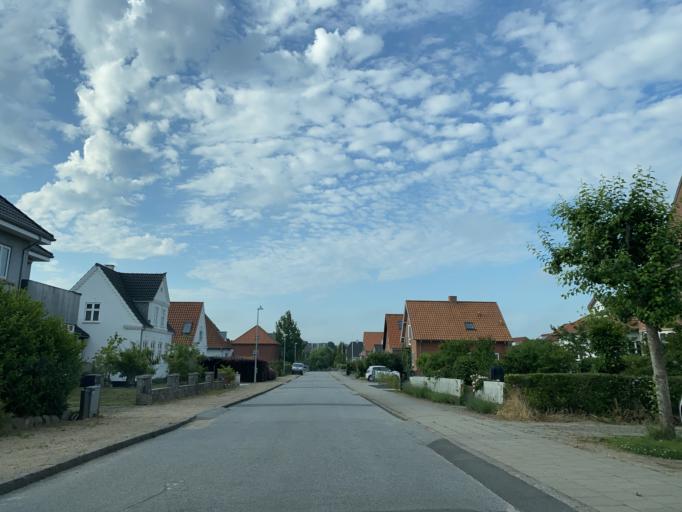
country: DK
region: South Denmark
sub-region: Haderslev Kommune
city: Haderslev
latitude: 55.2411
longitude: 9.4929
